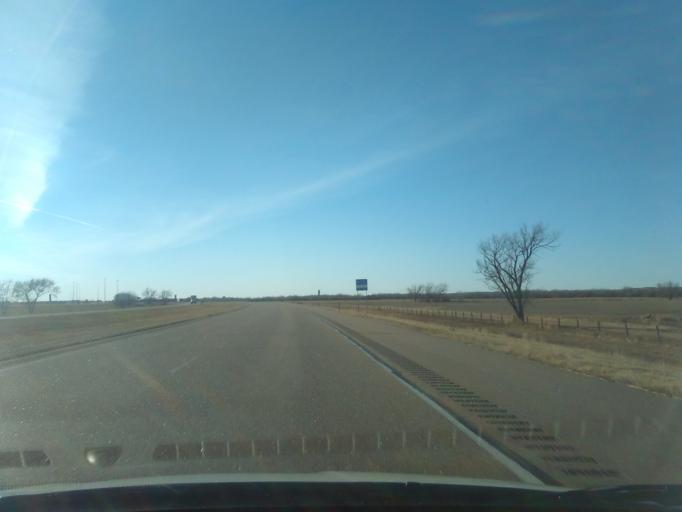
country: US
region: Colorado
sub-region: Sedgwick County
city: Julesburg
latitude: 41.0370
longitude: -102.1324
